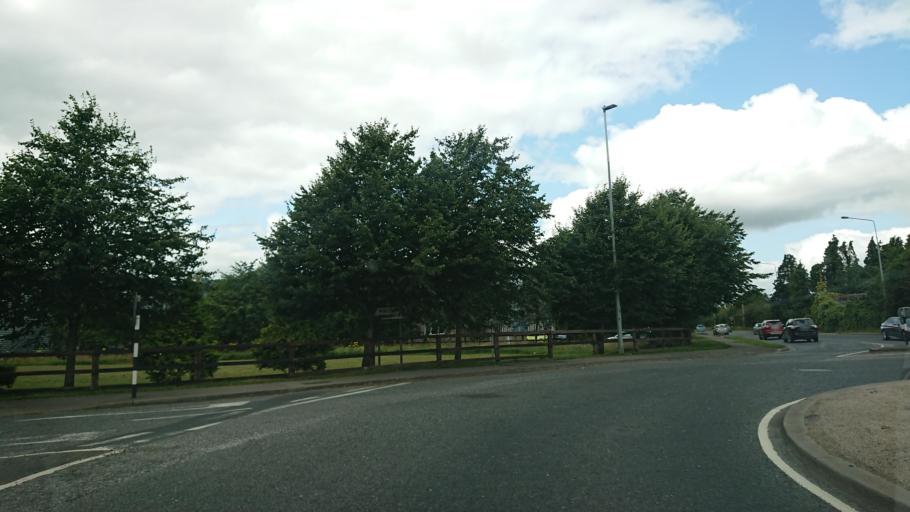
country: IE
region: Leinster
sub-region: Kildare
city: Johnstown
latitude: 53.2346
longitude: -6.6411
